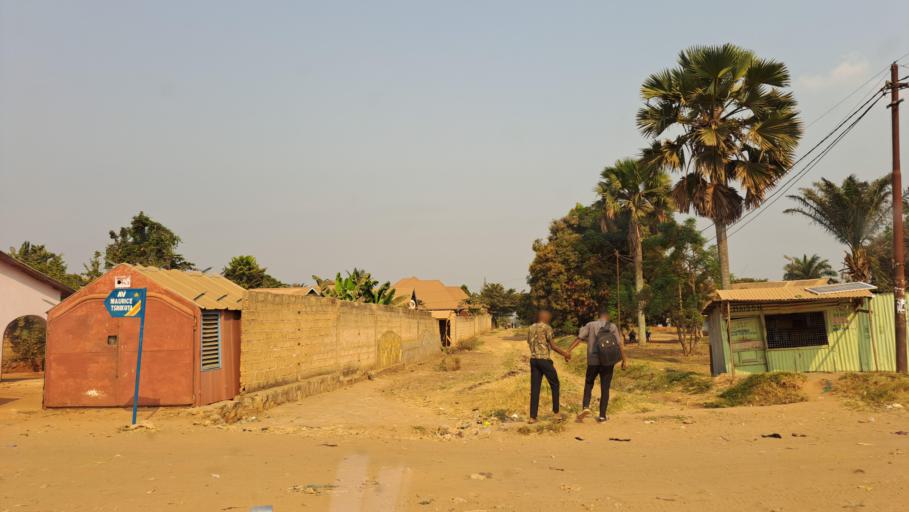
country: CD
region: Kasai-Oriental
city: Mbuji-Mayi
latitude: -6.1302
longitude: 23.5849
